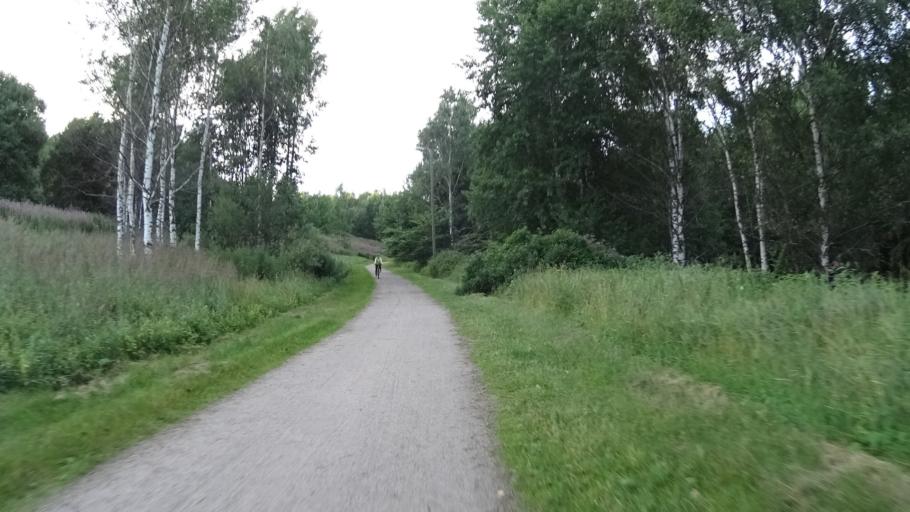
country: FI
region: Uusimaa
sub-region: Helsinki
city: Teekkarikylae
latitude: 60.2107
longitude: 24.8495
